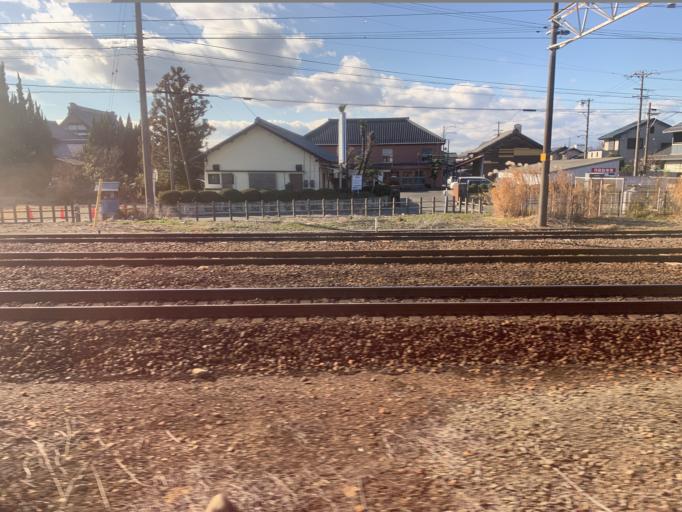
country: JP
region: Aichi
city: Kuroda
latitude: 35.3470
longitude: 136.7814
